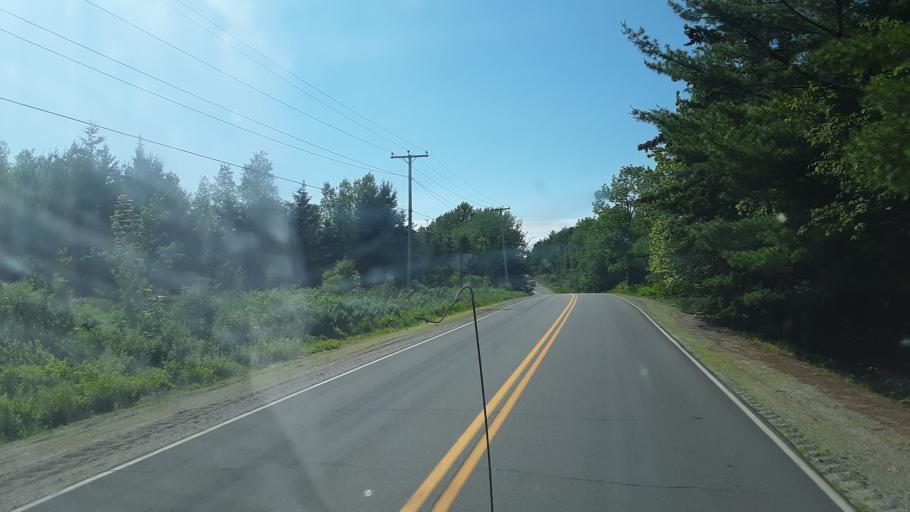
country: US
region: Maine
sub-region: Washington County
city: Cherryfield
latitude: 44.6191
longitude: -67.9295
